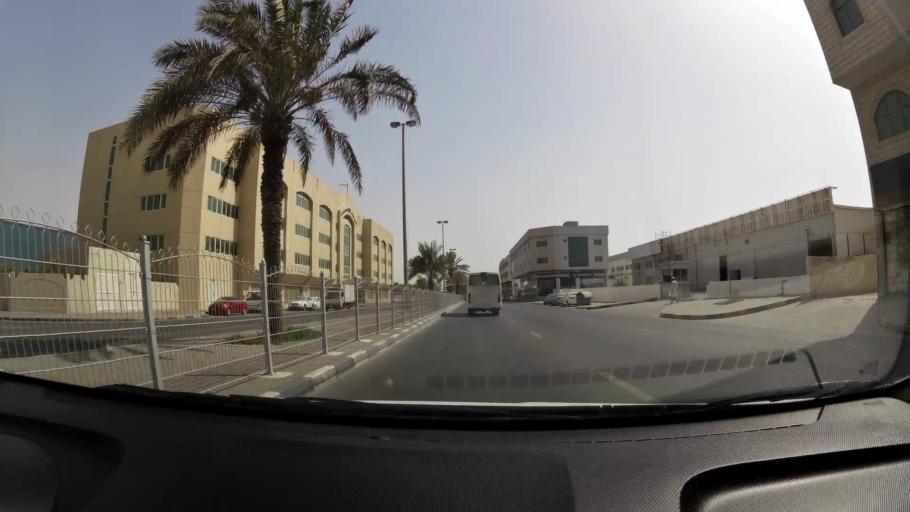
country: AE
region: Ash Shariqah
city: Sharjah
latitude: 25.3121
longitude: 55.4232
